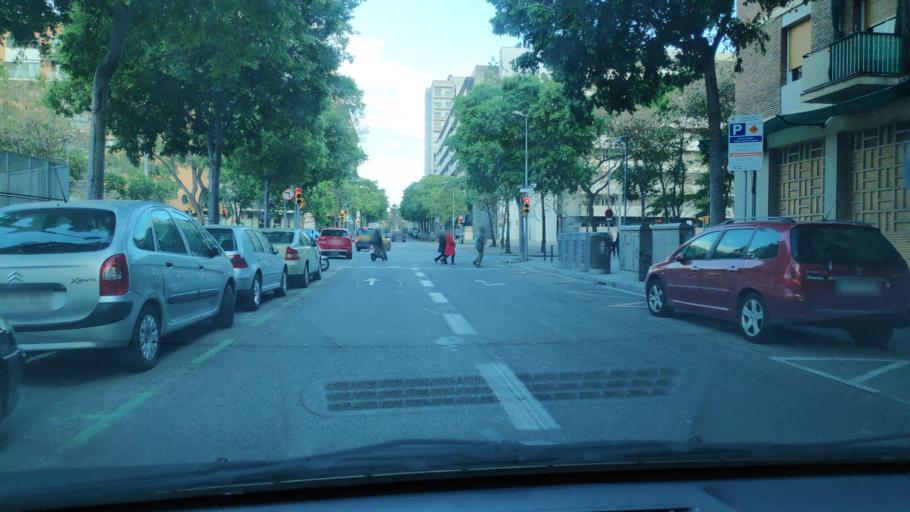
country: ES
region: Catalonia
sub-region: Provincia de Barcelona
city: Sant Marti
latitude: 41.4024
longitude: 2.2086
